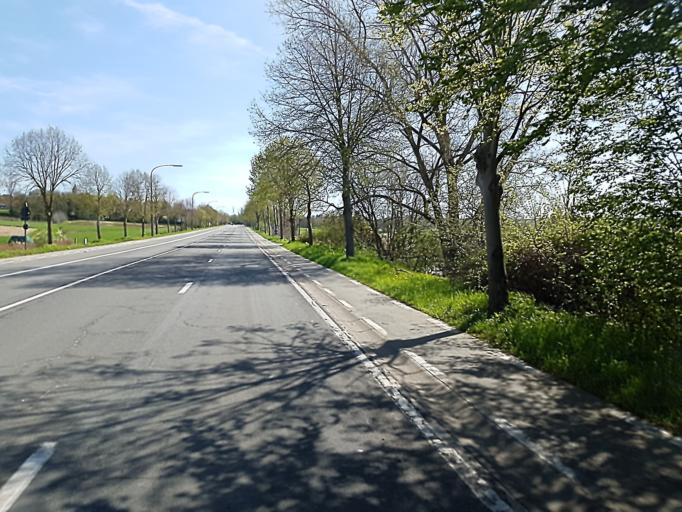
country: BE
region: Flanders
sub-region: Provincie West-Vlaanderen
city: Anzegem
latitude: 50.7814
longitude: 3.5182
